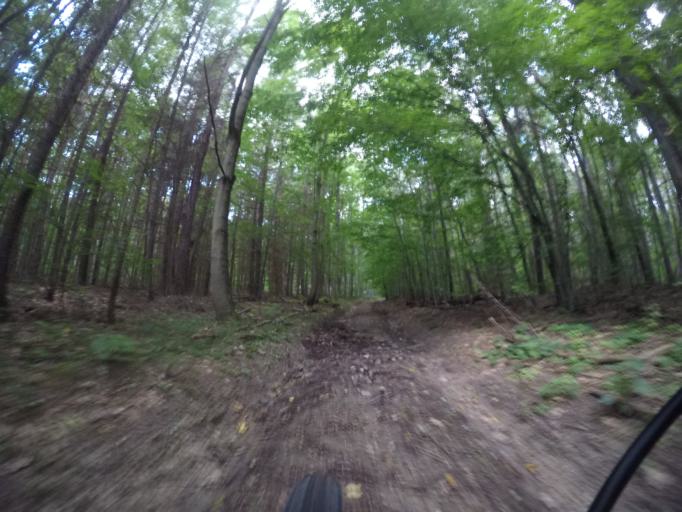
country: SK
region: Kosicky
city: Gelnica
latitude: 48.9238
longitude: 21.0336
